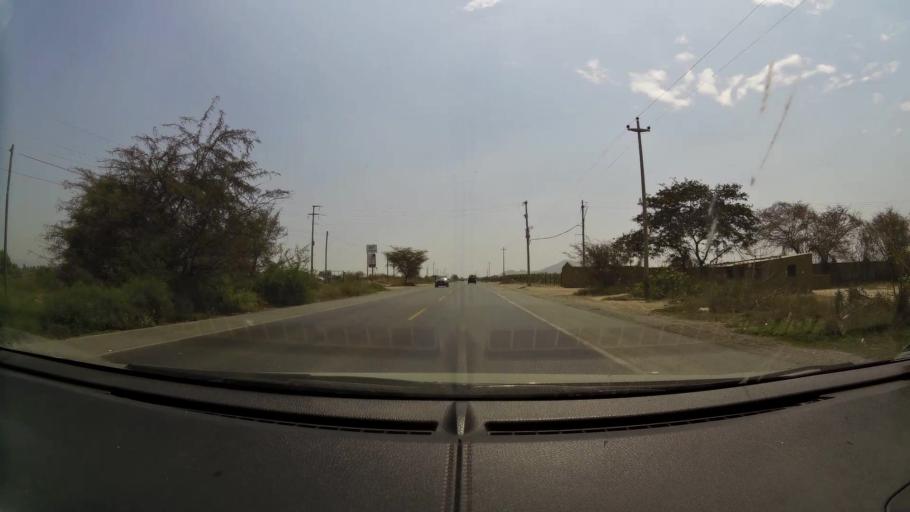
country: PE
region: La Libertad
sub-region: Chepen
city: Pacanga
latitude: -7.1364
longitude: -79.4673
